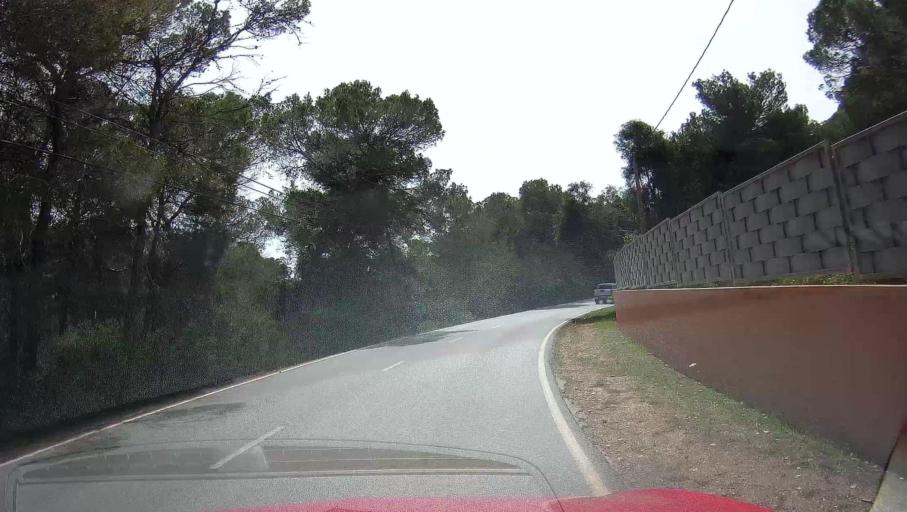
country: ES
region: Balearic Islands
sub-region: Illes Balears
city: Santa Eularia des Riu
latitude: 39.0075
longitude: 1.5701
